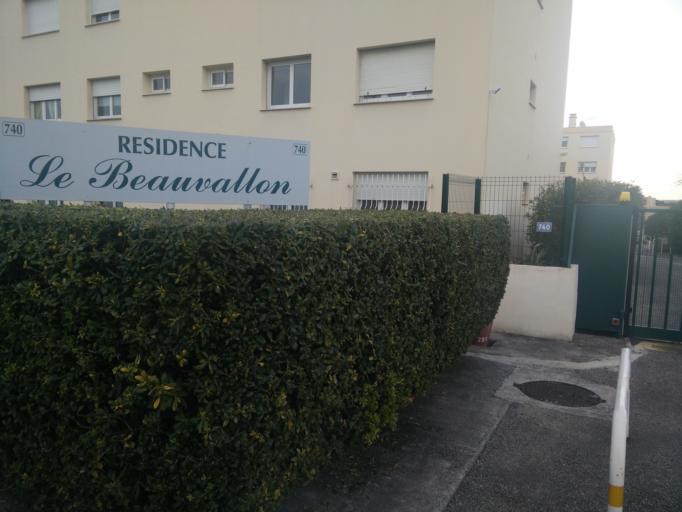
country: FR
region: Provence-Alpes-Cote d'Azur
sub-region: Departement des Alpes-Maritimes
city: Antibes
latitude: 43.5937
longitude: 7.1152
